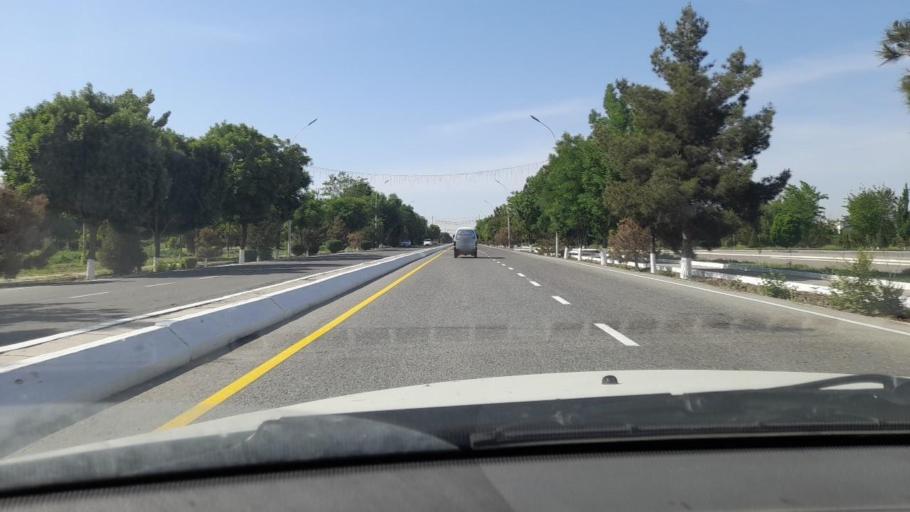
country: UZ
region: Bukhara
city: Bukhara
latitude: 39.7975
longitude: 64.4354
